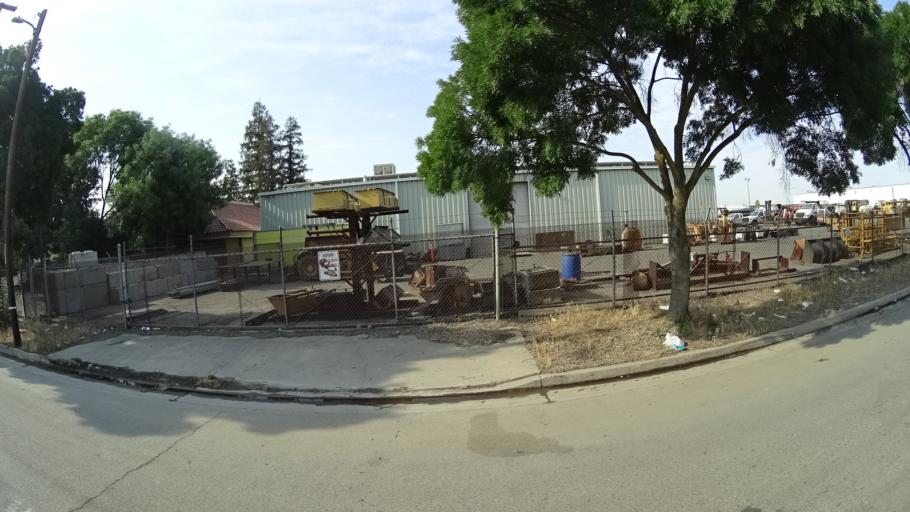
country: US
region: California
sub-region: Fresno County
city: Fresno
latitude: 36.7476
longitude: -119.8137
